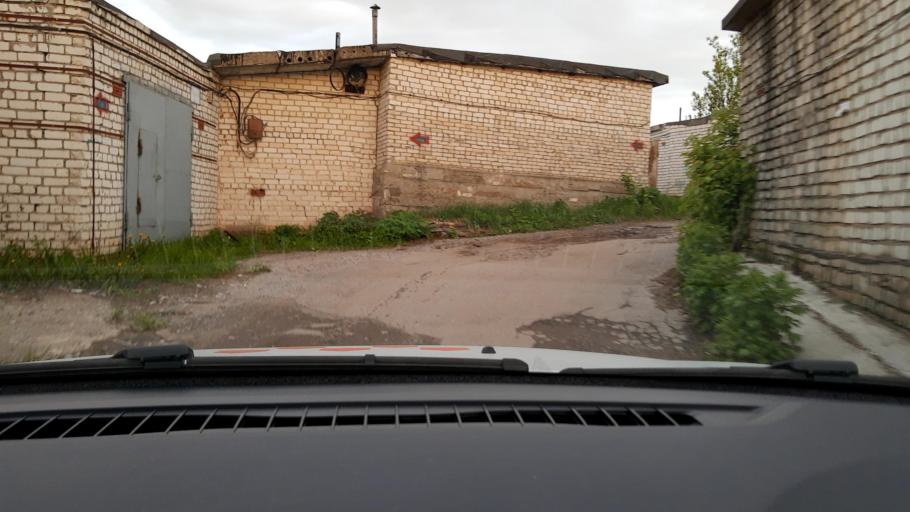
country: RU
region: Nizjnij Novgorod
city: Afonino
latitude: 56.3095
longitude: 44.0843
